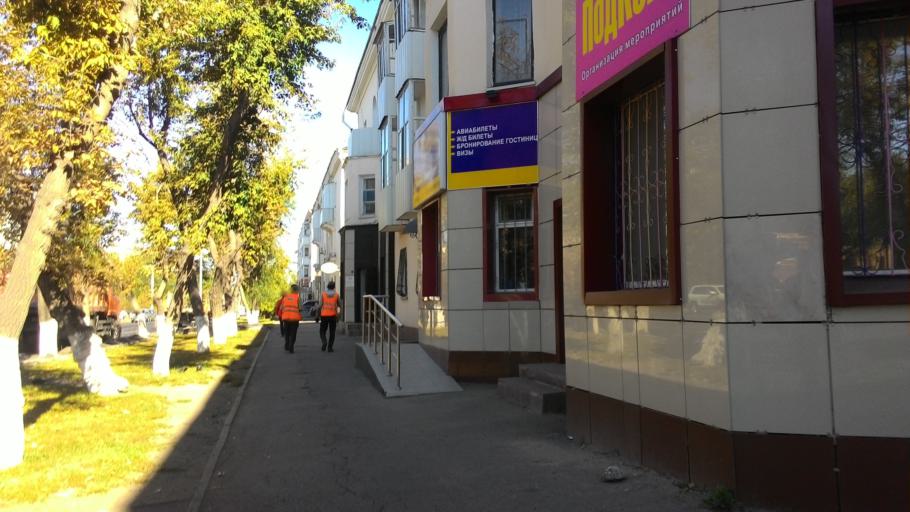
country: KZ
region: Astana Qalasy
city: Astana
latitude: 51.1687
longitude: 71.4158
